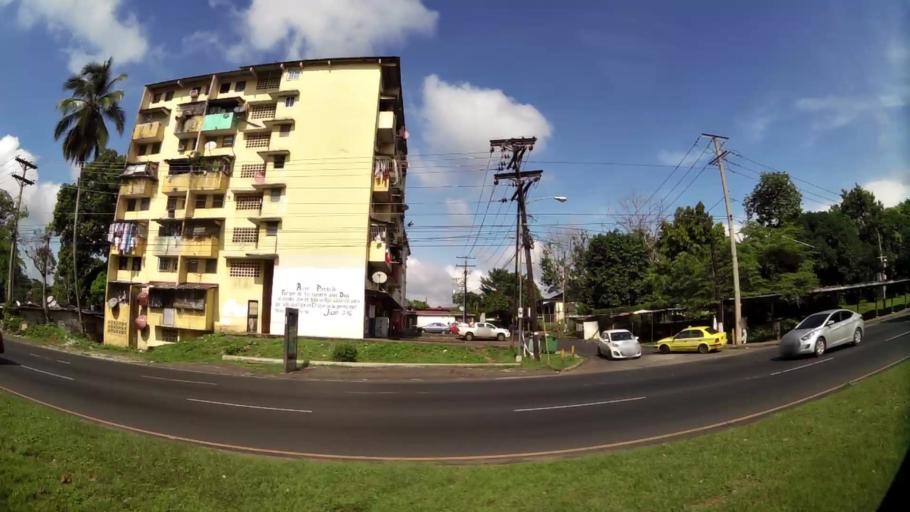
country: PA
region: Panama
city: Panama
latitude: 8.9840
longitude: -79.5355
